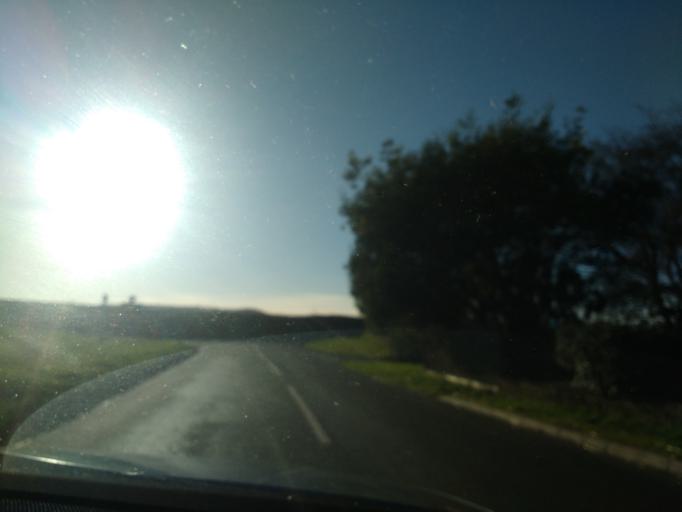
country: GB
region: England
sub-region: Isle of Wight
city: Newchurch
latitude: 50.6426
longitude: -1.2081
